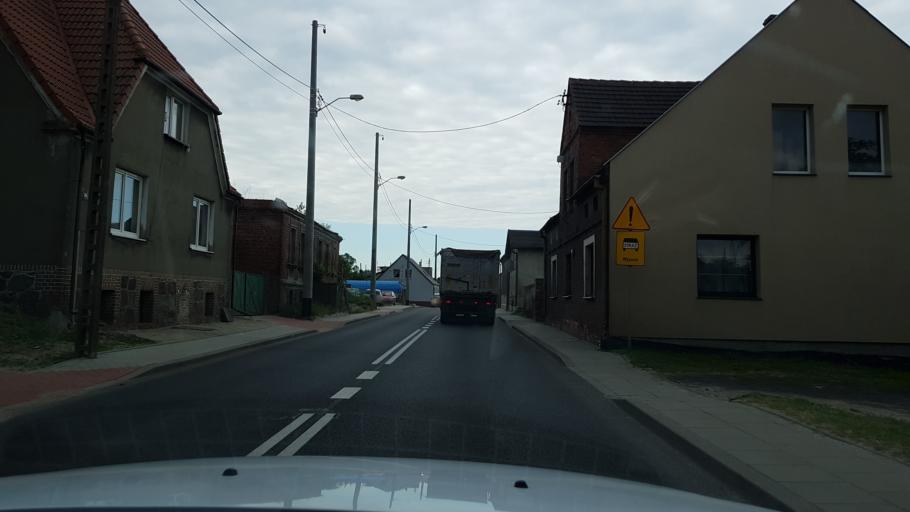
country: PL
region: West Pomeranian Voivodeship
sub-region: Powiat policki
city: Przeclaw
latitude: 53.3226
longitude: 14.5386
